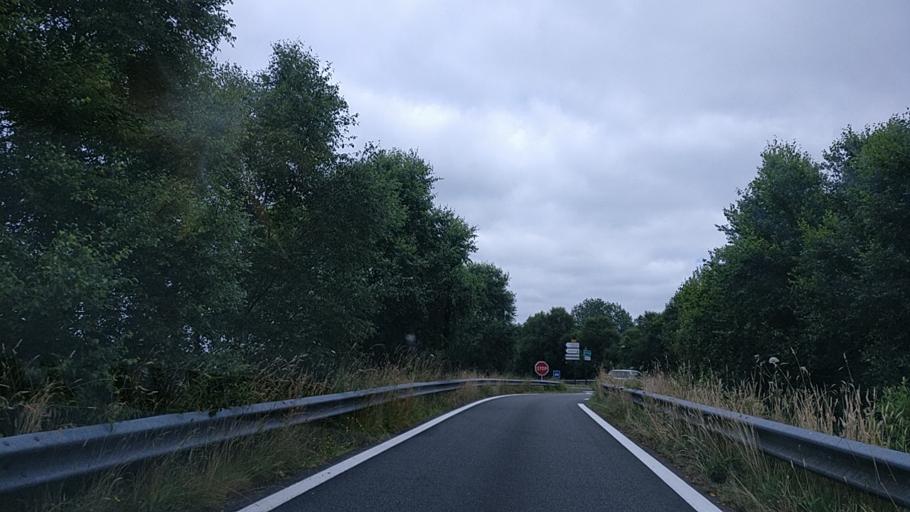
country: FR
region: Brittany
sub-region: Departement des Cotes-d'Armor
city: Belle-Isle-en-Terre
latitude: 48.5523
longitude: -3.3734
